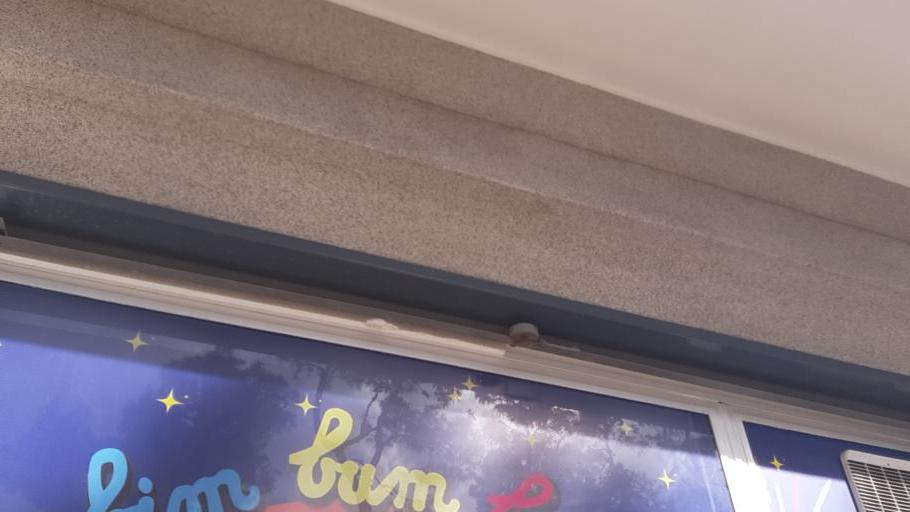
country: IT
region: Apulia
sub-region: Provincia di Barletta - Andria - Trani
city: Andria
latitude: 41.2326
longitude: 16.2963
